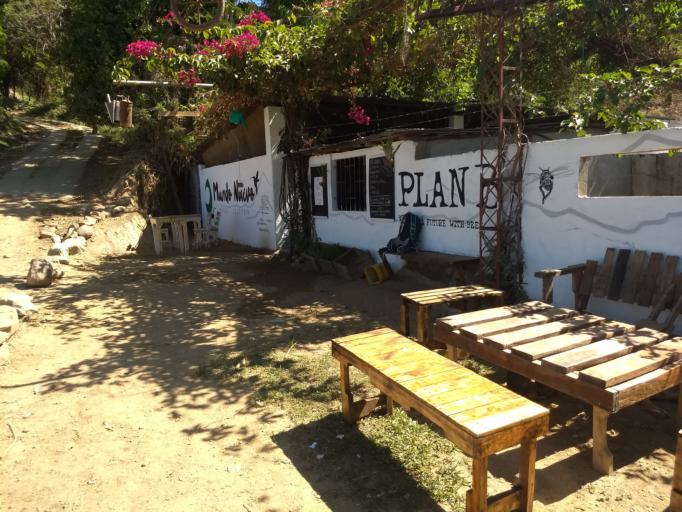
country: CO
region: Magdalena
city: Santa Marta
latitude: 11.1514
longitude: -74.1074
